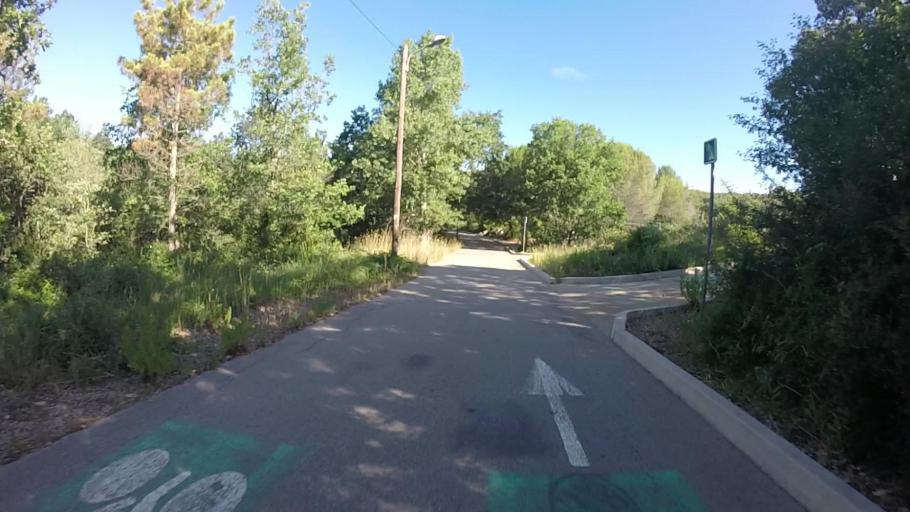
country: FR
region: Provence-Alpes-Cote d'Azur
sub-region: Departement des Alpes-Maritimes
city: Biot
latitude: 43.6237
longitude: 7.0550
